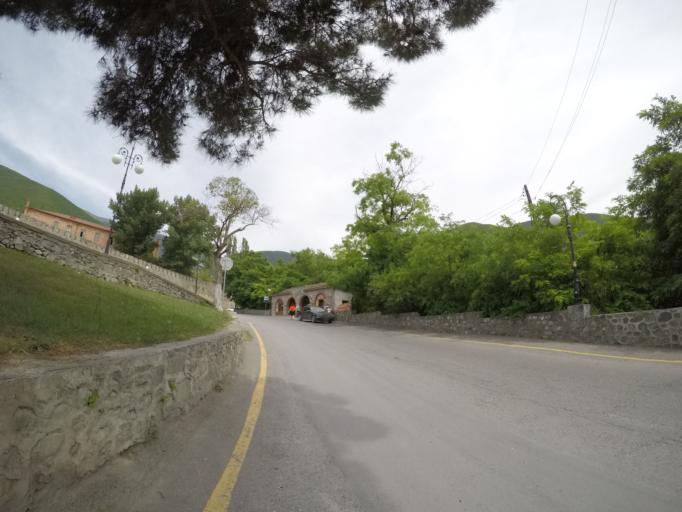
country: AZ
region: Shaki City
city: Sheki
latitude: 41.2023
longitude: 47.1958
